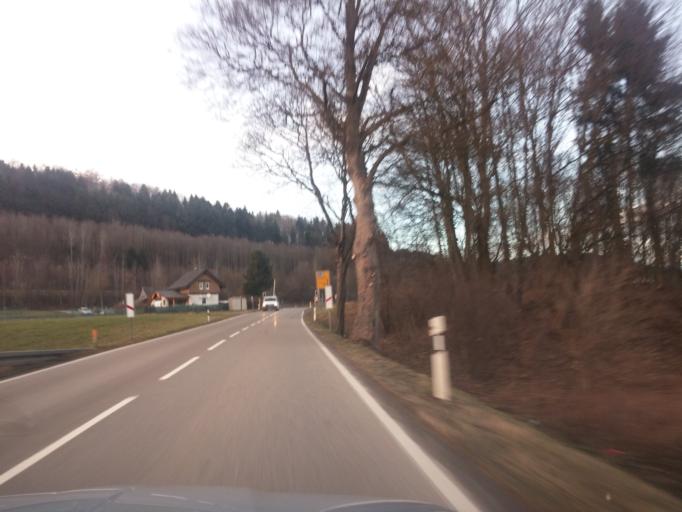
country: DE
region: Baden-Wuerttemberg
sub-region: Tuebingen Region
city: Aichstetten
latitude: 47.8766
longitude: 10.0371
